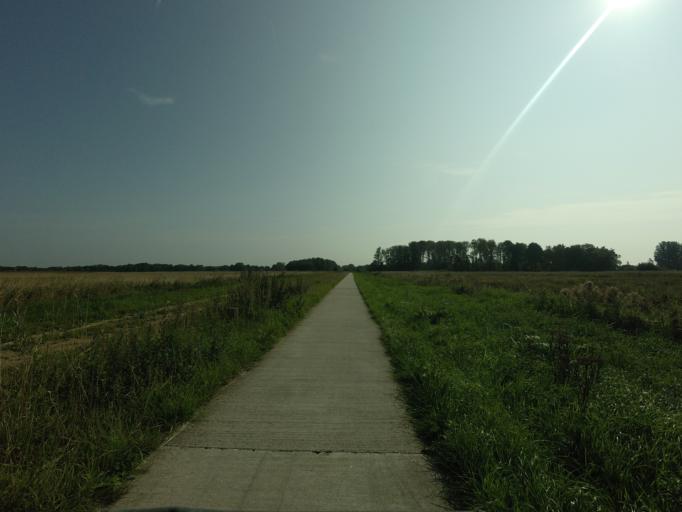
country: NL
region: Groningen
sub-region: Gemeente Groningen
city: Groningen
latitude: 53.1552
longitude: 6.5336
